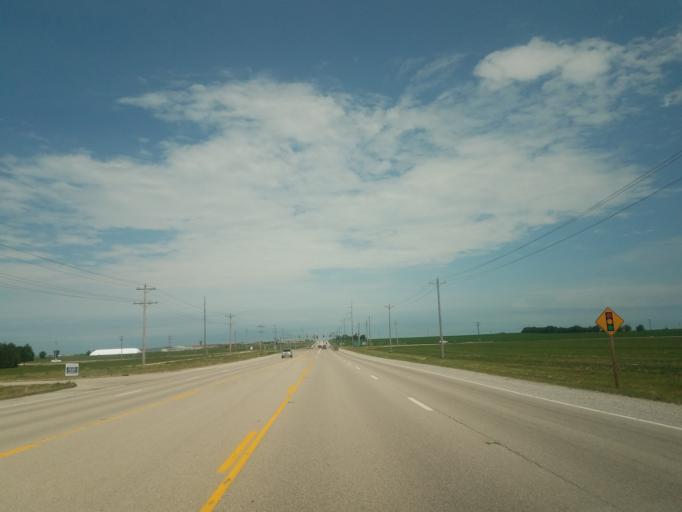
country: US
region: Illinois
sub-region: McLean County
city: Downs
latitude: 40.4559
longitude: -88.9018
